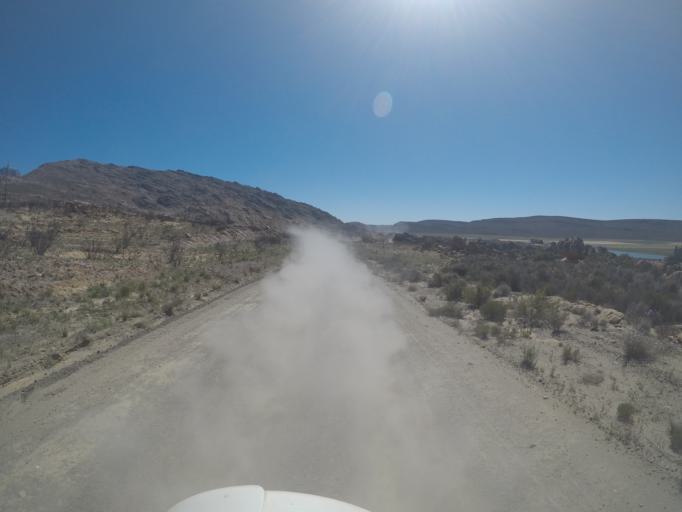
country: ZA
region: Western Cape
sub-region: Cape Winelands District Municipality
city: Ceres
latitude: -32.8511
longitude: 19.4456
